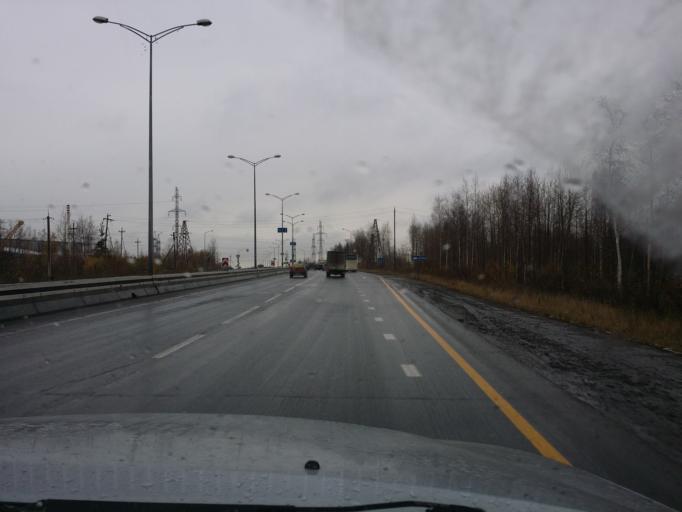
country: RU
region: Khanty-Mansiyskiy Avtonomnyy Okrug
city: Nizhnevartovsk
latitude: 60.9875
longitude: 76.4646
